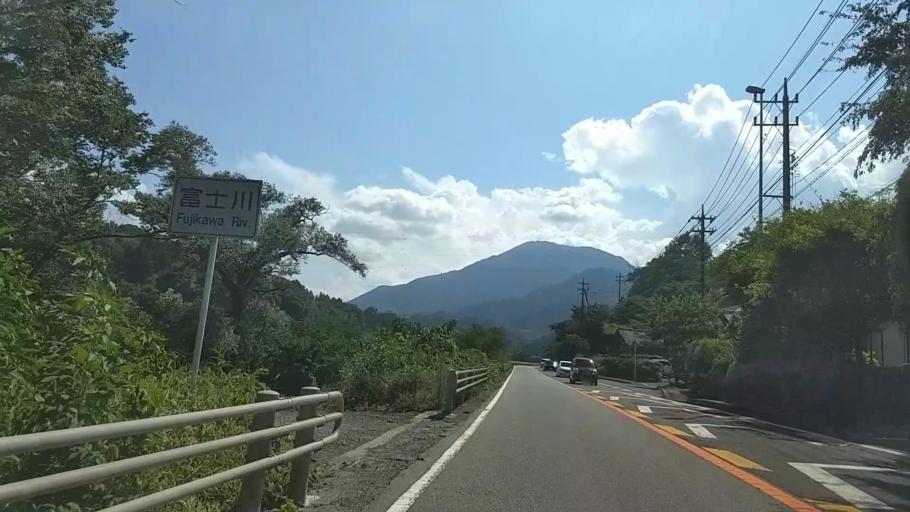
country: JP
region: Yamanashi
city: Ryuo
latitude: 35.4460
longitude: 138.4413
